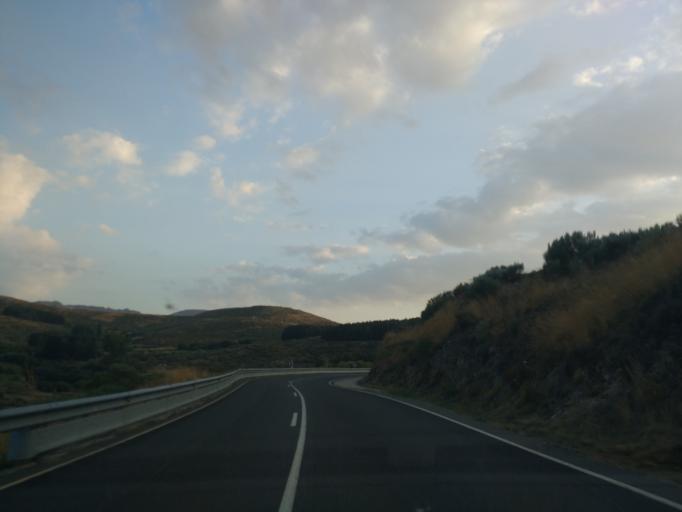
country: ES
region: Castille and Leon
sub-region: Provincia de Avila
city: San Martin del Pimpollar
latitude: 40.3687
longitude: -5.0438
